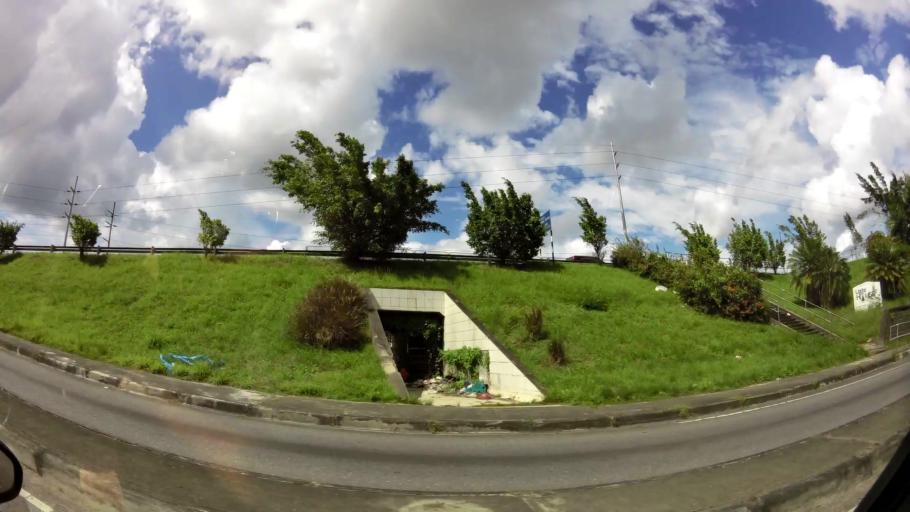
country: TT
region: City of San Fernando
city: San Fernando
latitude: 10.2606
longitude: -61.4609
